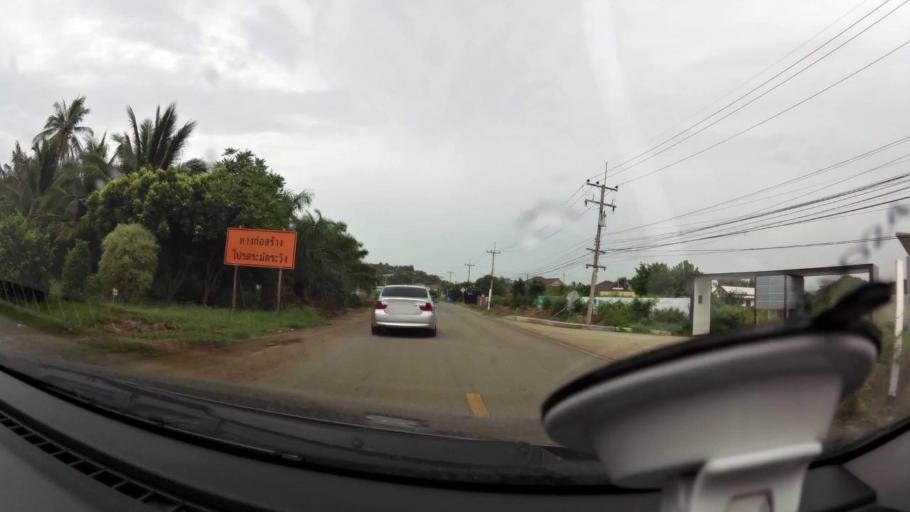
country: TH
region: Prachuap Khiri Khan
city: Pran Buri
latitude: 12.4147
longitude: 99.9563
